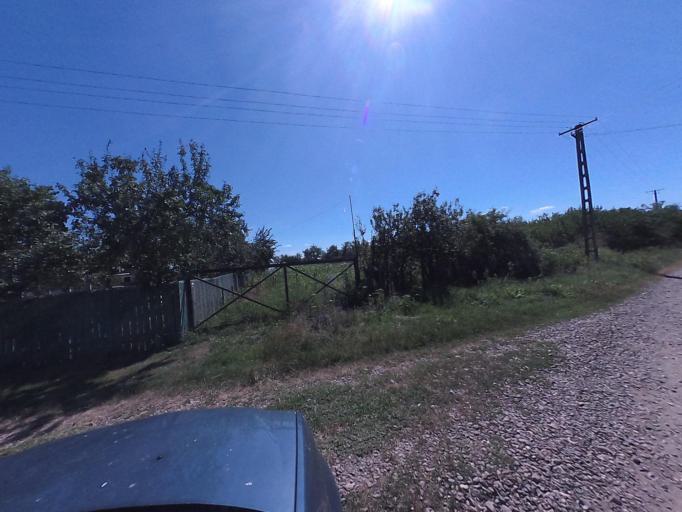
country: RO
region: Vaslui
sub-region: Comuna Costesti
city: Costesti
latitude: 46.4796
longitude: 27.7849
